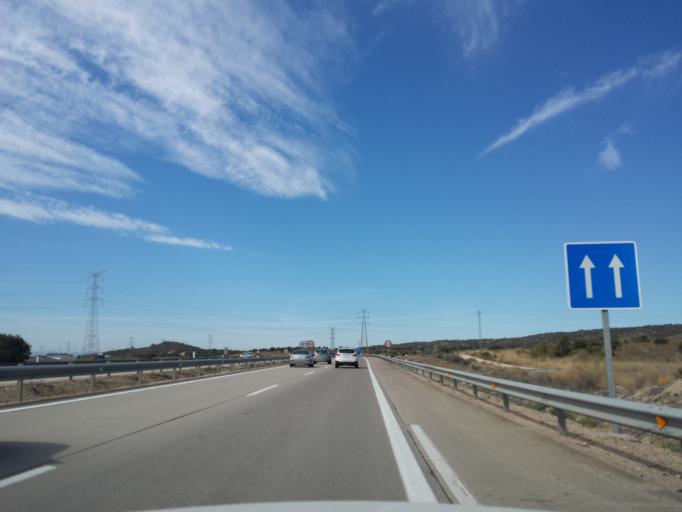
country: ES
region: Castille-La Mancha
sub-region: Province of Toledo
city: Talavera de la Reina
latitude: 40.0058
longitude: -4.8234
